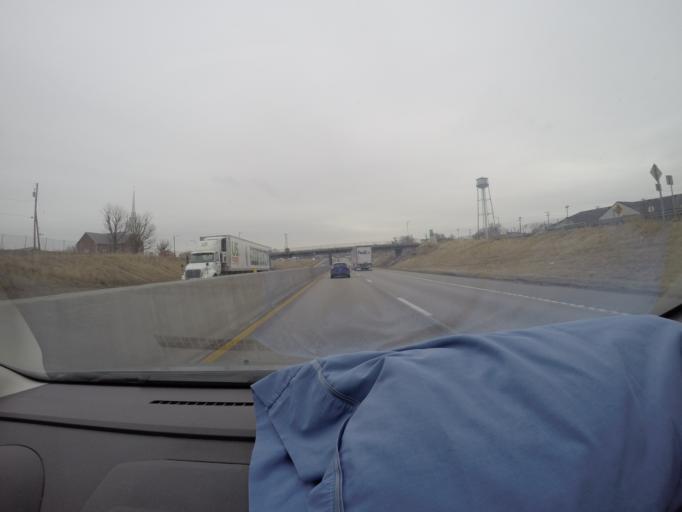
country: US
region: Missouri
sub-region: Warren County
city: Wright City
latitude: 38.8299
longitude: -91.0218
